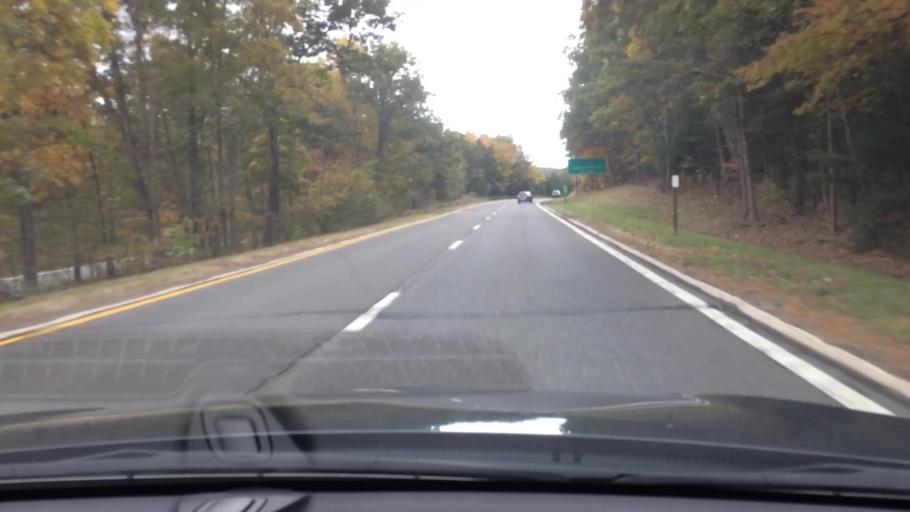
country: US
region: New York
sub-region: Dutchess County
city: Pine Plains
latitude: 42.0216
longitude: -73.7337
